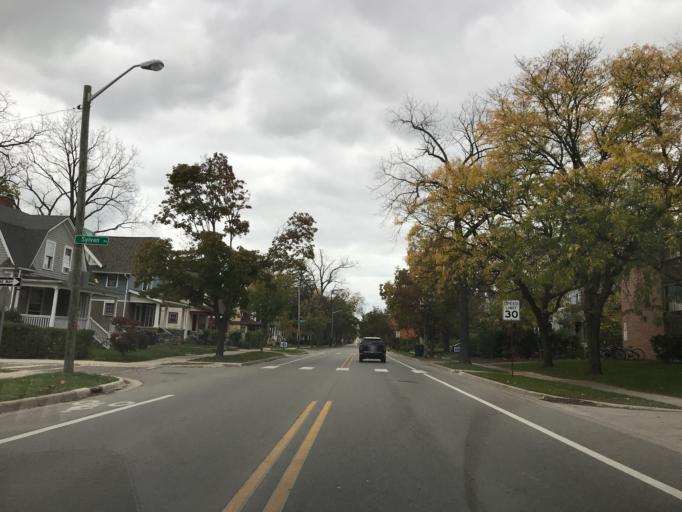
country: US
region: Michigan
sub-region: Washtenaw County
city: Ann Arbor
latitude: 42.2667
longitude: -83.7361
